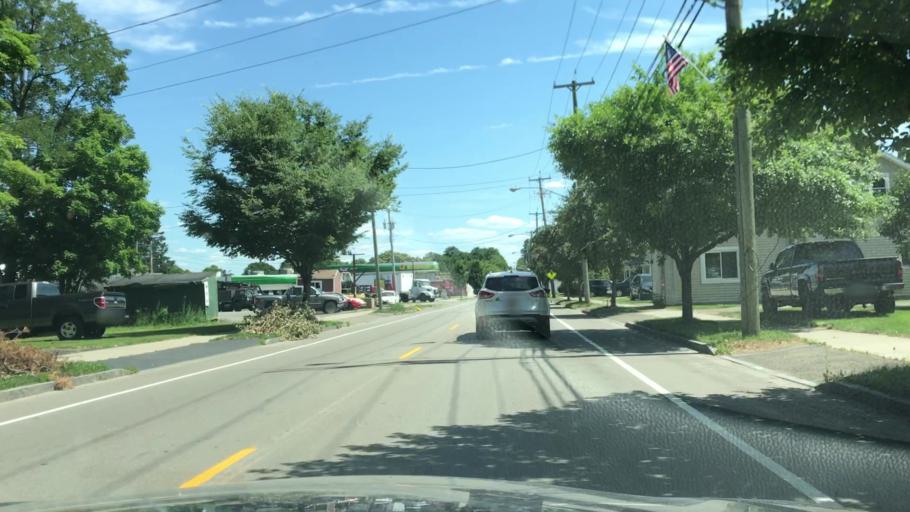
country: US
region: New York
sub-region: Livingston County
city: Mount Morris
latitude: 42.7325
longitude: -77.8782
